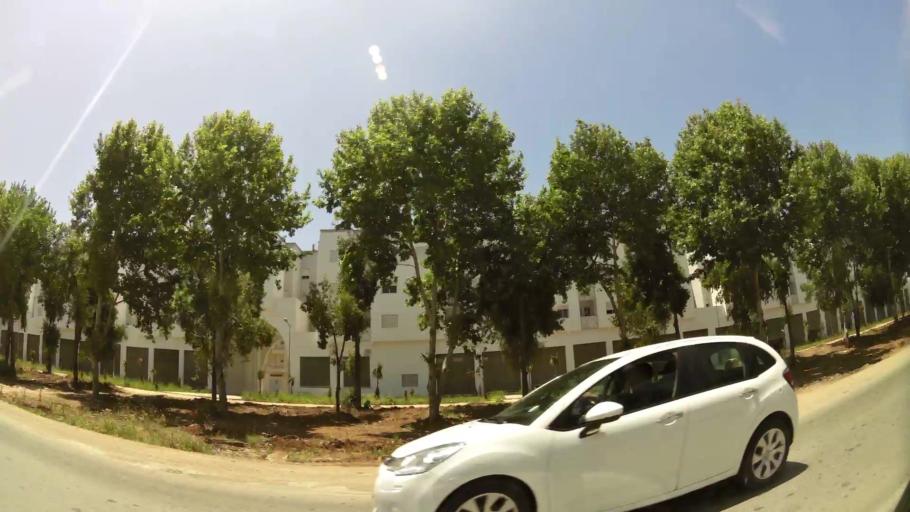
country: MA
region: Fes-Boulemane
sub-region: Fes
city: Fes
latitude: 34.0387
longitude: -5.0338
